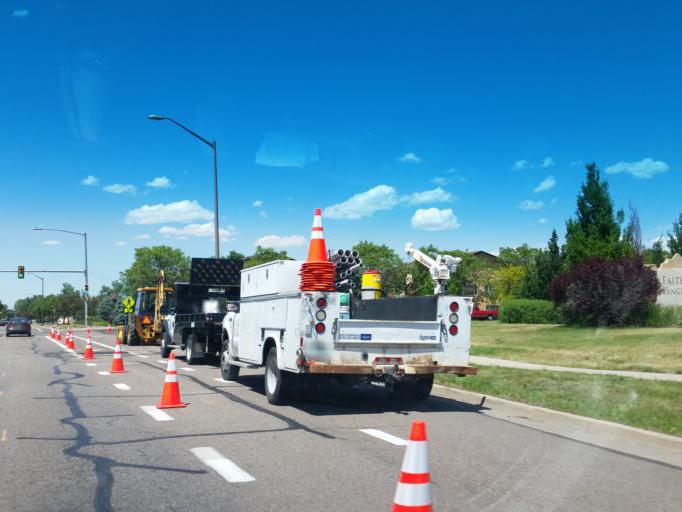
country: US
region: Colorado
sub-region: Larimer County
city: Fort Collins
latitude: 40.5336
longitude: -105.0960
